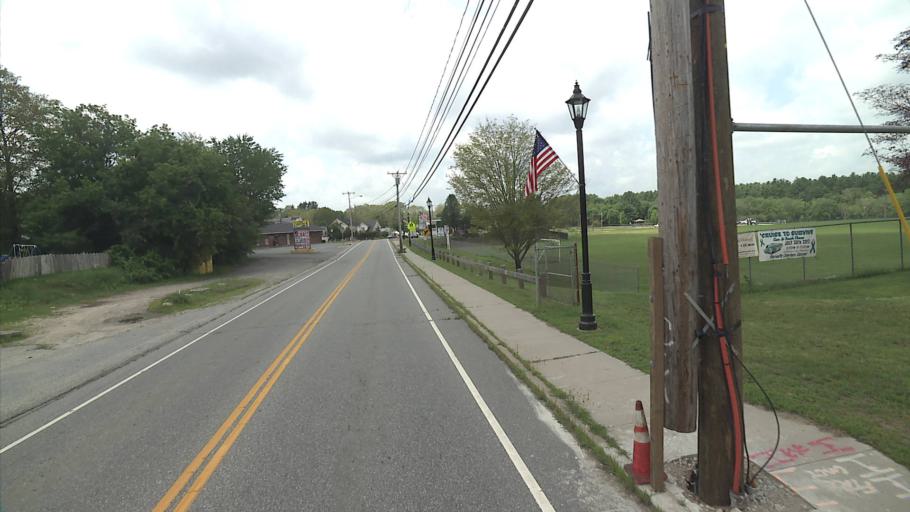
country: US
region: Connecticut
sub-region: Windham County
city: Plainfield
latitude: 41.5734
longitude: -71.8666
